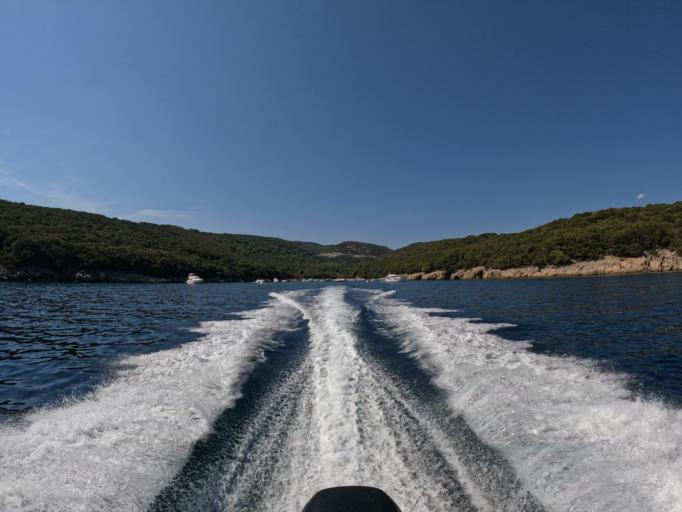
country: HR
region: Primorsko-Goranska
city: Cres
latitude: 44.9495
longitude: 14.4637
